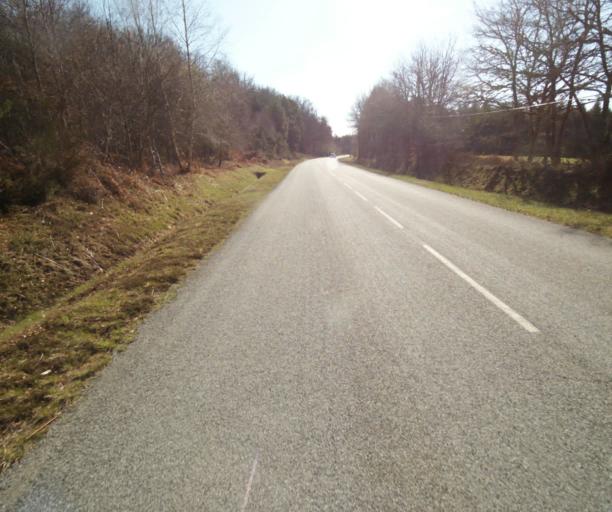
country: FR
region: Limousin
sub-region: Departement de la Correze
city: Correze
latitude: 45.2801
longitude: 1.9348
